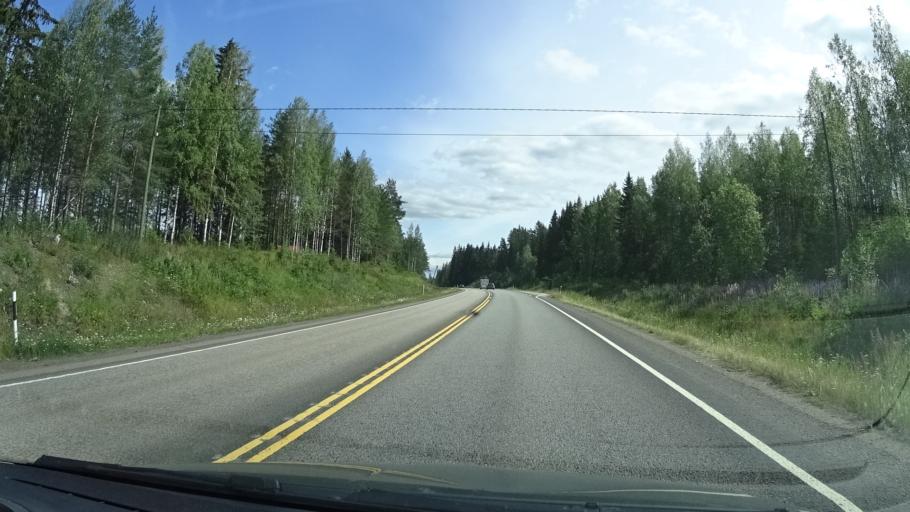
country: FI
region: Central Finland
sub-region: Jyvaeskylae
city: Muurame
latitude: 62.2667
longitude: 25.4997
